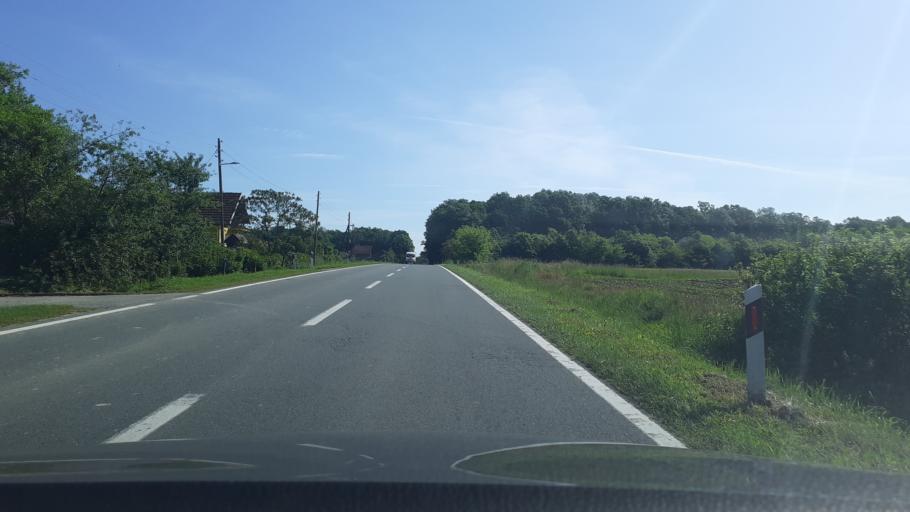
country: HR
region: Brodsko-Posavska
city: Batrina
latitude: 45.2019
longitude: 17.6723
